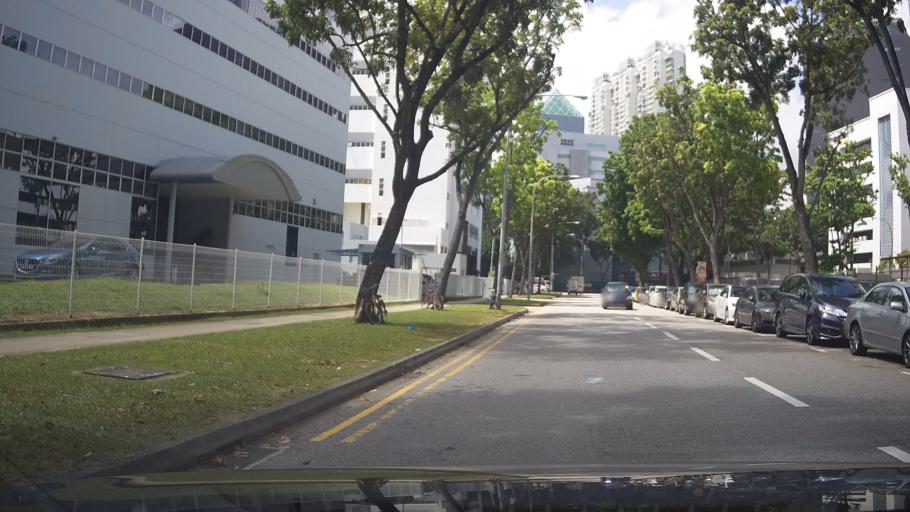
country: SG
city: Singapore
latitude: 1.3104
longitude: 103.8670
